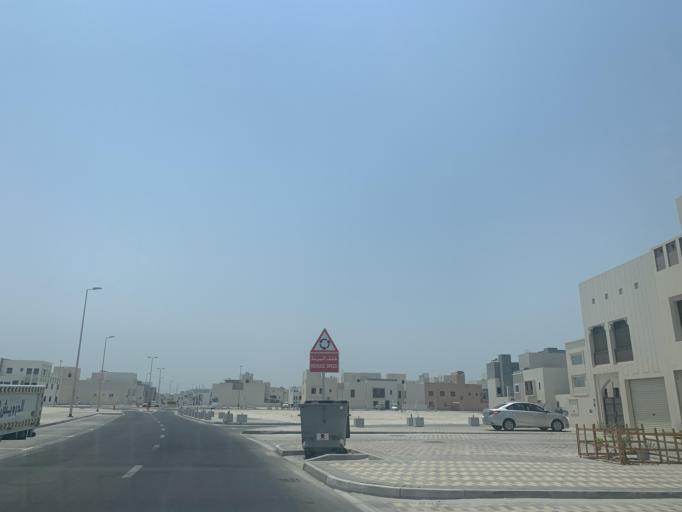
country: BH
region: Muharraq
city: Al Hadd
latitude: 26.2344
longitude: 50.6754
